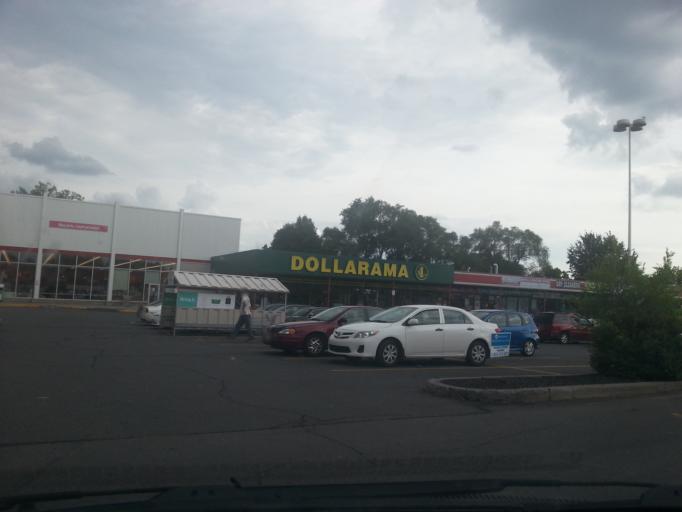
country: CA
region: Ontario
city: Ottawa
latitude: 45.4417
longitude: -75.6438
